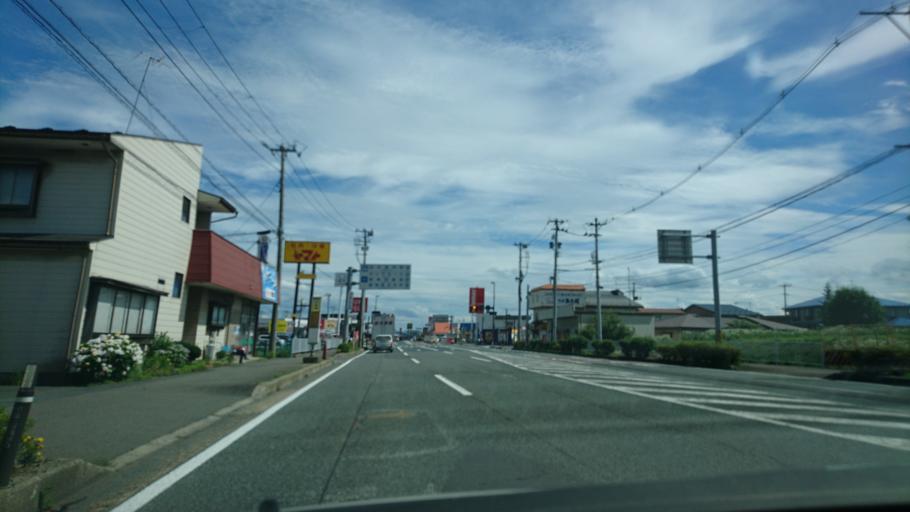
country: JP
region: Iwate
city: Morioka-shi
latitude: 39.6560
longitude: 141.1631
